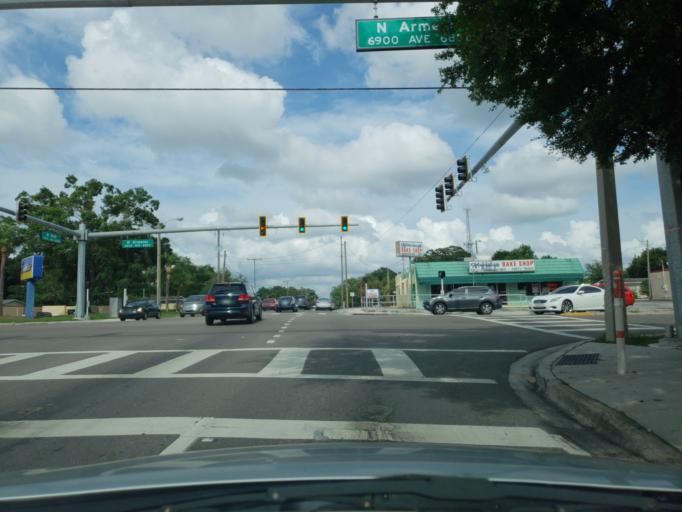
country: US
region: Florida
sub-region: Hillsborough County
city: Egypt Lake-Leto
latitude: 28.0107
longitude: -82.4846
